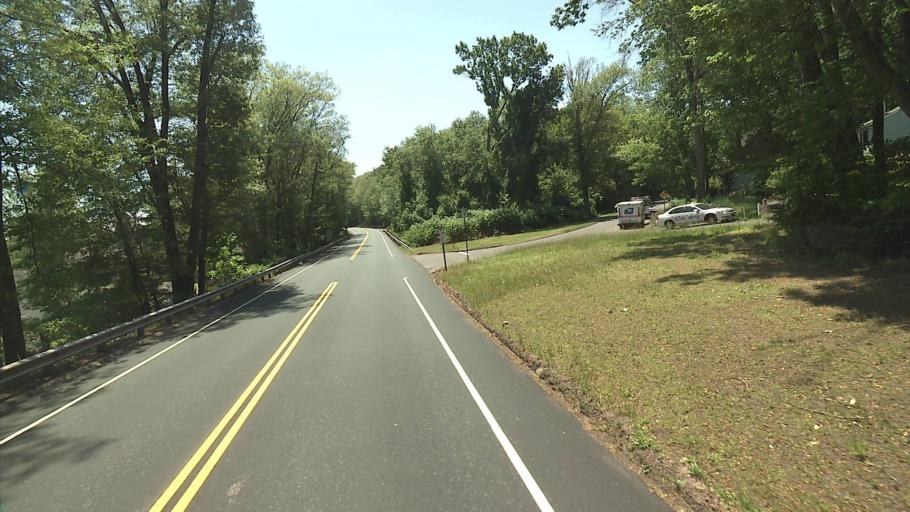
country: US
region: Connecticut
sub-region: Tolland County
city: Crystal Lake
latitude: 41.9401
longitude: -72.3783
